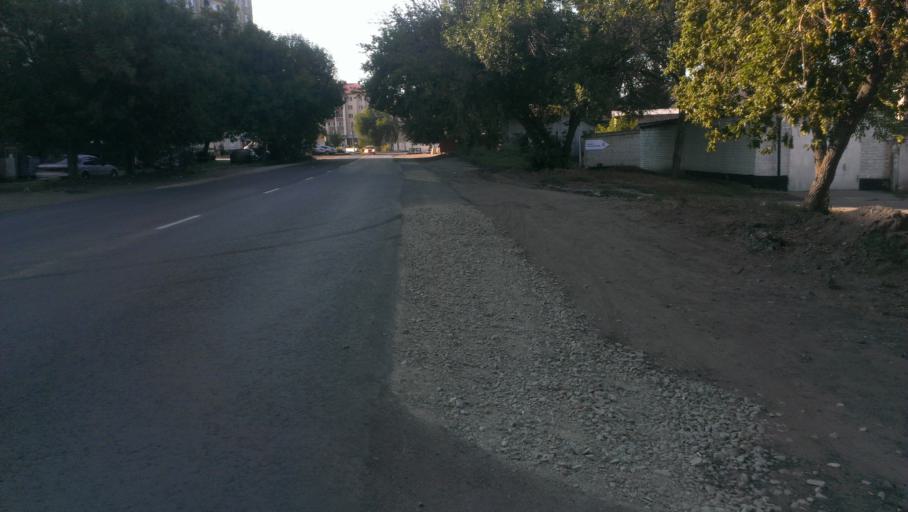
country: RU
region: Altai Krai
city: Novosilikatnyy
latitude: 53.3070
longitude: 83.6239
